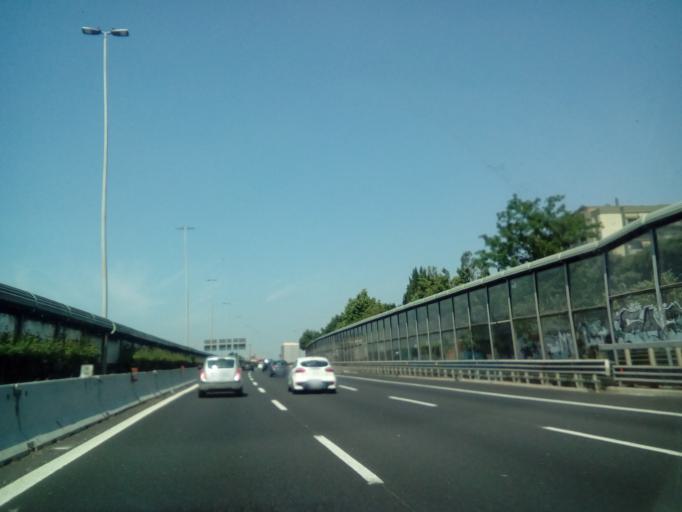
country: IT
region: Latium
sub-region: Citta metropolitana di Roma Capitale
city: Vitinia
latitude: 41.8030
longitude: 12.4367
